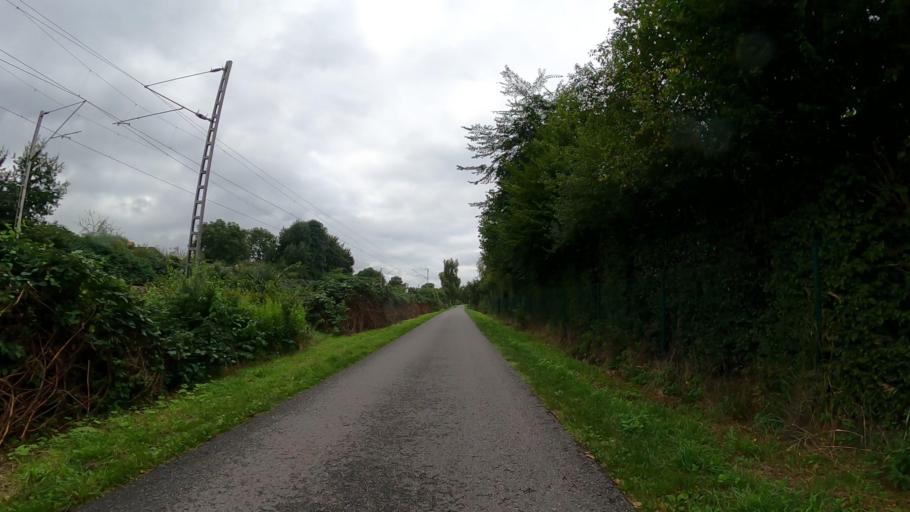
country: DE
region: Lower Saxony
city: Neu Wulmstorf
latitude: 53.4726
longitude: 9.7775
